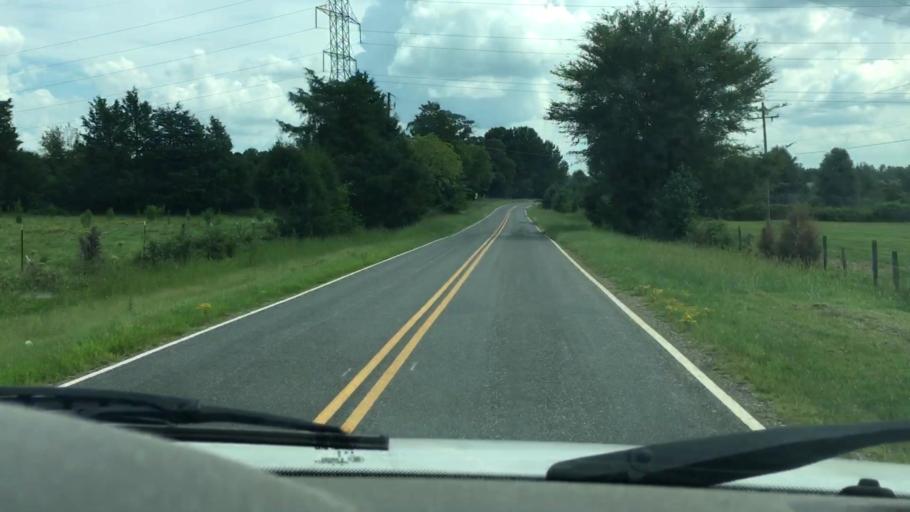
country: US
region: North Carolina
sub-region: Iredell County
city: Troutman
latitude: 35.6796
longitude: -80.8505
